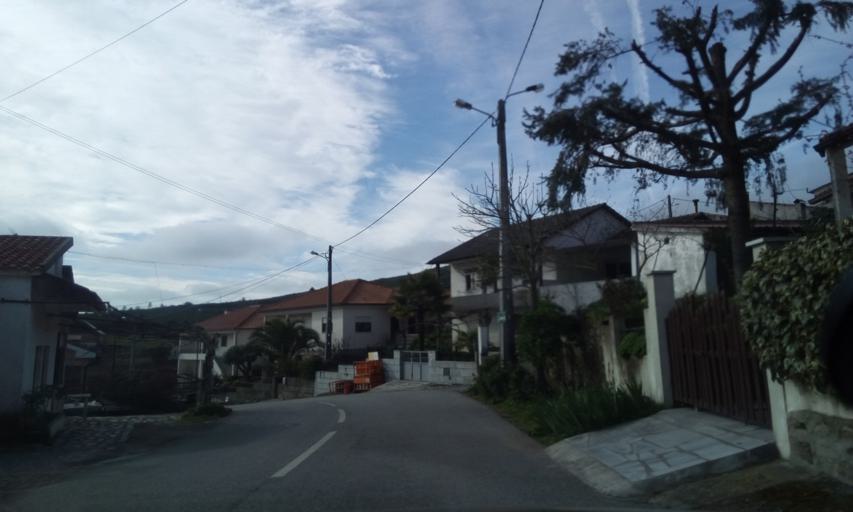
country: PT
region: Guarda
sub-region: Fornos de Algodres
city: Fornos de Algodres
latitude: 40.6833
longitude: -7.5338
